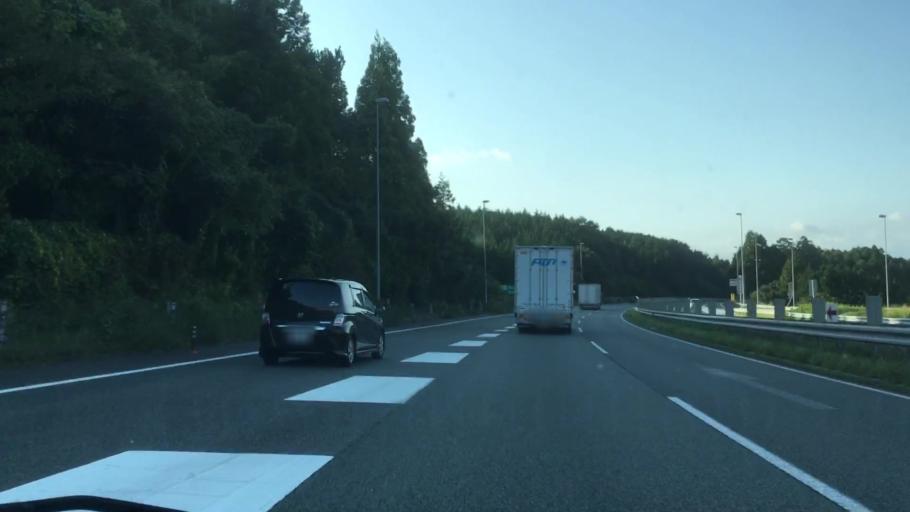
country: JP
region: Yamaguchi
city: Ogori-shimogo
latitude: 34.1546
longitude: 131.3352
